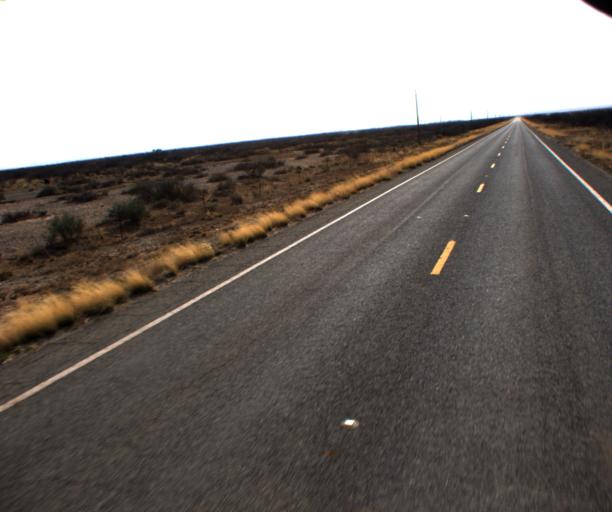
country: US
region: Arizona
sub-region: Cochise County
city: Willcox
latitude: 32.1953
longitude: -109.7280
